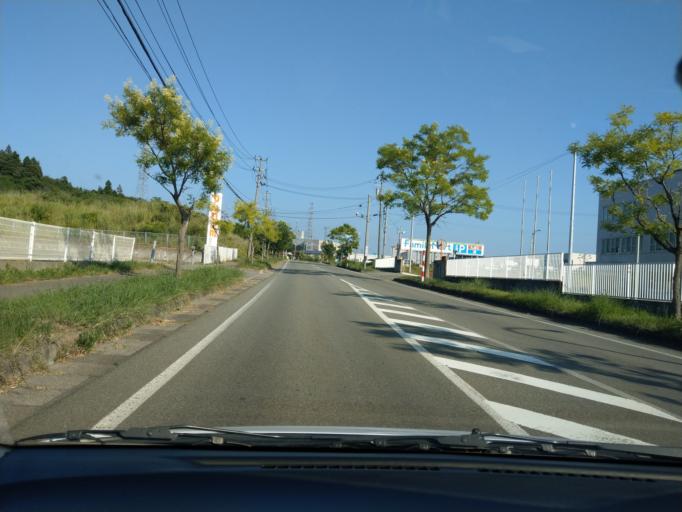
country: JP
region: Akita
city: Akita
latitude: 39.6594
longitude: 140.1715
